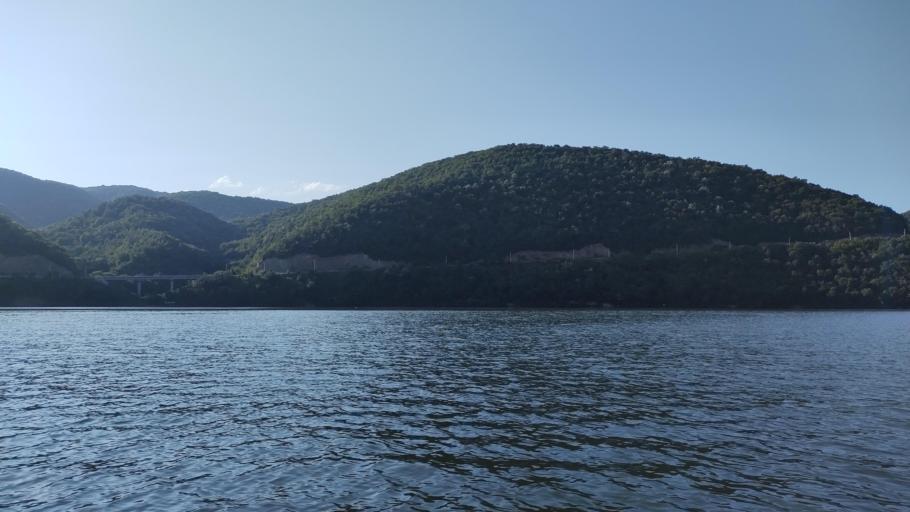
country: RO
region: Mehedinti
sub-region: Comuna Dubova
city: Dubova
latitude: 44.5838
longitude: 22.2521
